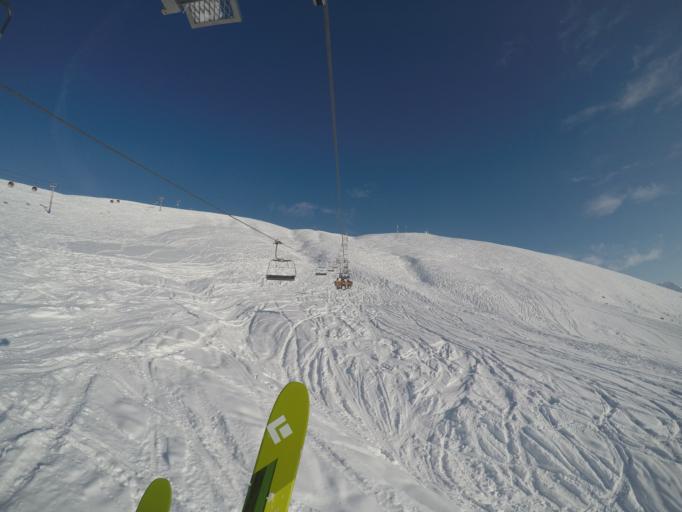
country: GE
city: Gudauri
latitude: 42.4827
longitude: 44.4948
